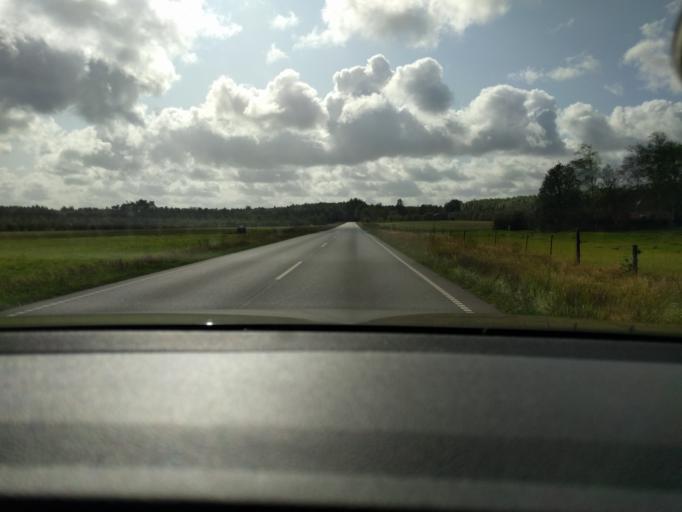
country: DK
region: Central Jutland
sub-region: Viborg Kommune
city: Bjerringbro
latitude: 56.2884
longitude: 9.6528
